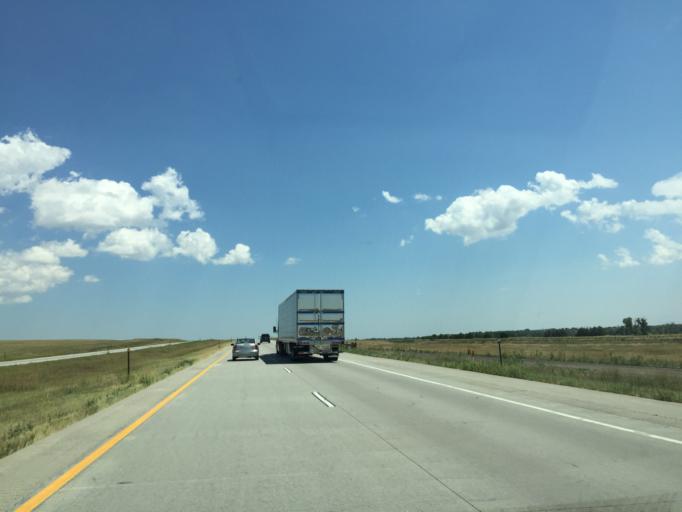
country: US
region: Colorado
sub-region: Lincoln County
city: Limon
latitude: 39.2833
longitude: -103.7769
